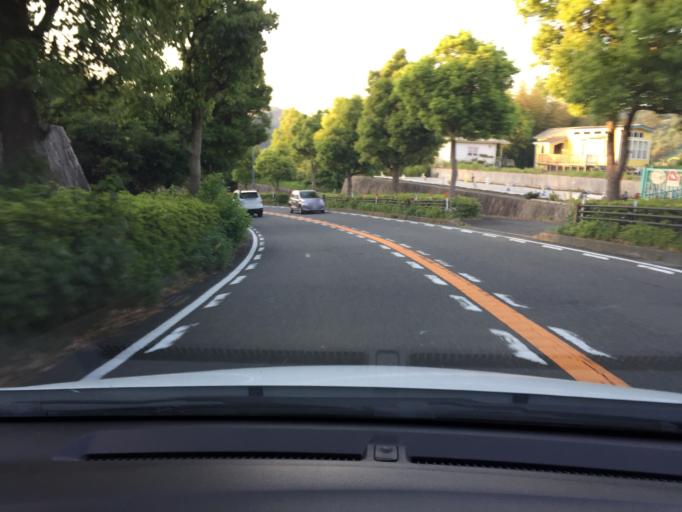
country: JP
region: Kanagawa
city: Hayama
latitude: 35.2644
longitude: 139.6099
